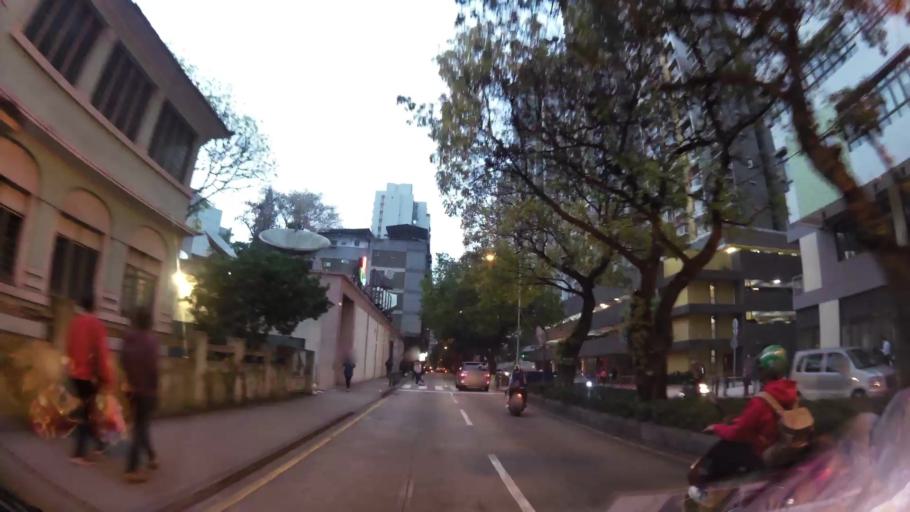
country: MO
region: Macau
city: Macau
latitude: 22.2056
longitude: 113.5491
